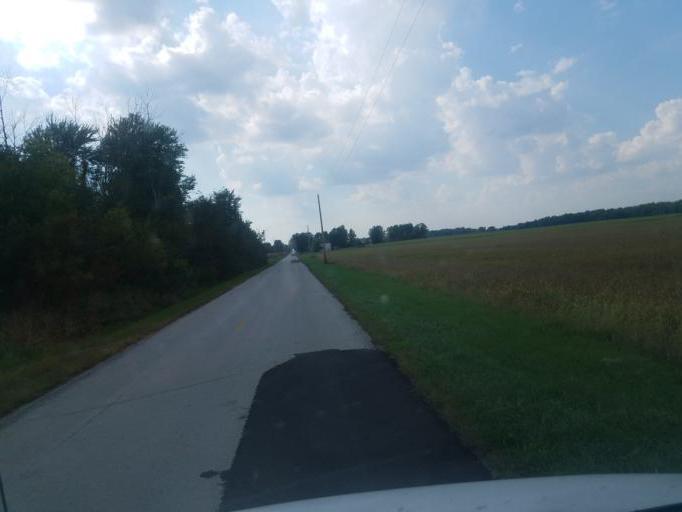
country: US
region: Ohio
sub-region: Hardin County
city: Kenton
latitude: 40.7459
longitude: -83.6059
